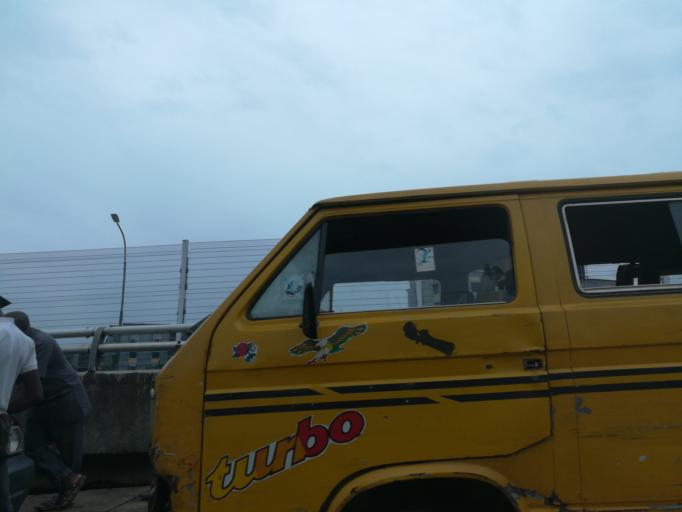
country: NG
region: Lagos
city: Makoko
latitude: 6.4926
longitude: 3.3866
